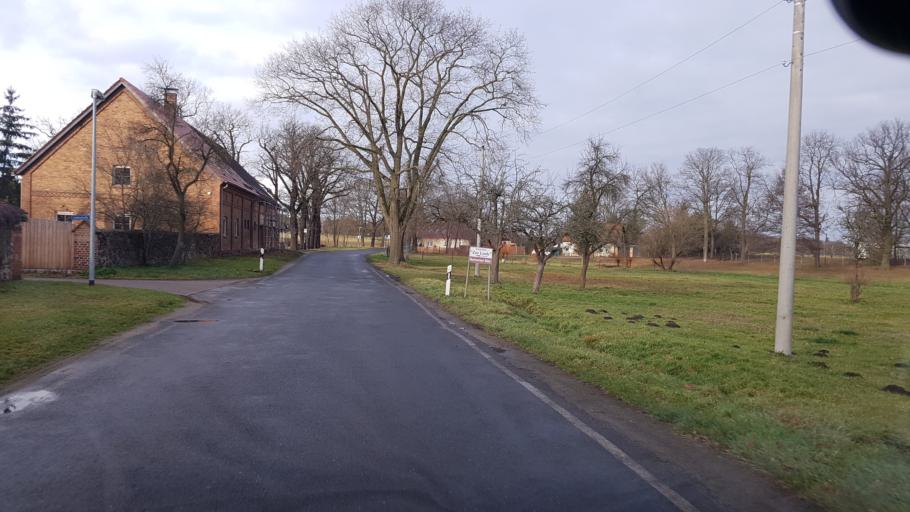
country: DE
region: Brandenburg
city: Altdobern
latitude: 51.6635
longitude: 13.9948
